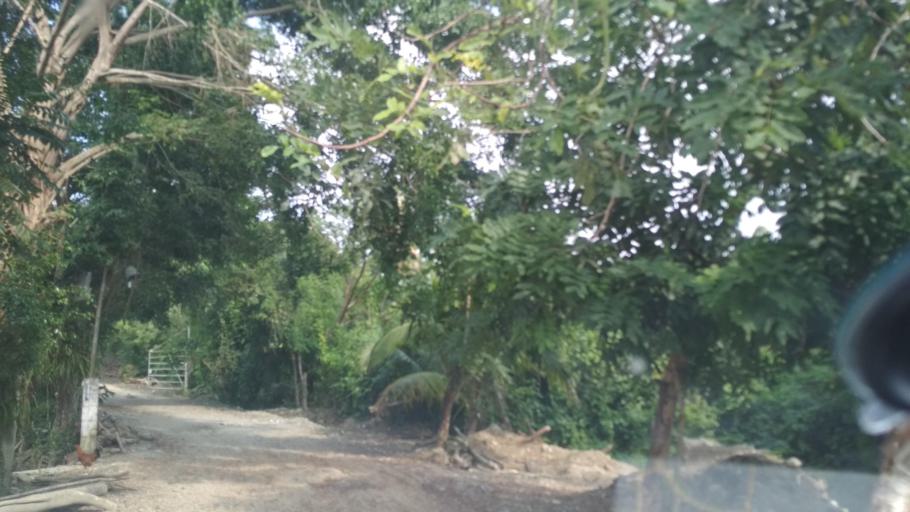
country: MX
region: Veracruz
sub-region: Poza Rica de Hidalgo
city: El Mollejon
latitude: 20.5172
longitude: -97.3787
